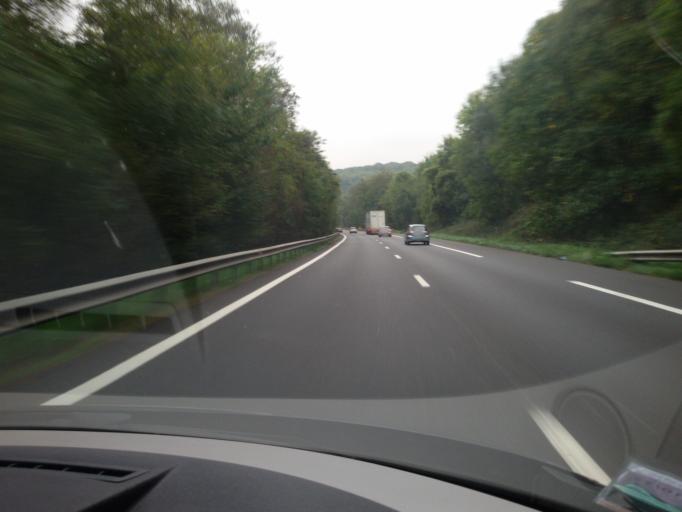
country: FR
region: Ile-de-France
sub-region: Departement de l'Essonne
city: Marcoussis
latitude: 48.6319
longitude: 2.2269
